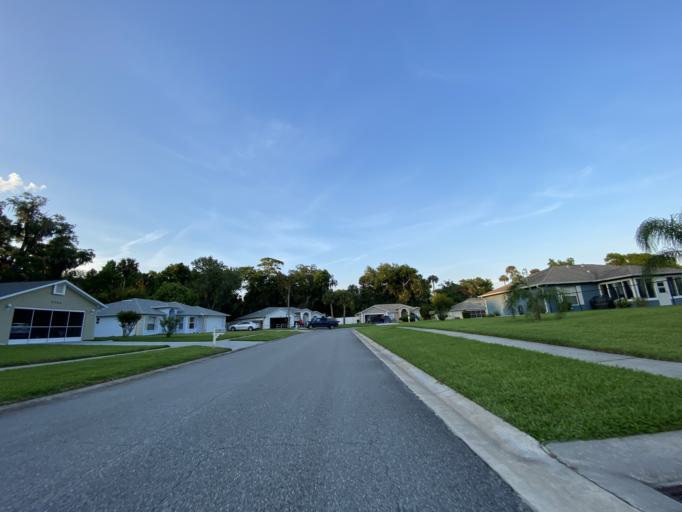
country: US
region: Florida
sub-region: Volusia County
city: Port Orange
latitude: 29.1434
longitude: -81.0059
